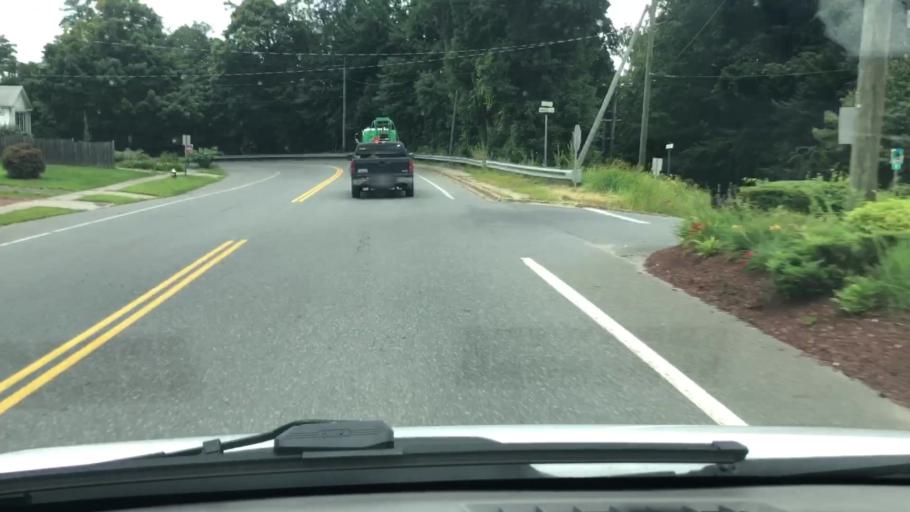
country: US
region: Massachusetts
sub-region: Franklin County
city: Turners Falls
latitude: 42.6043
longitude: -72.5509
